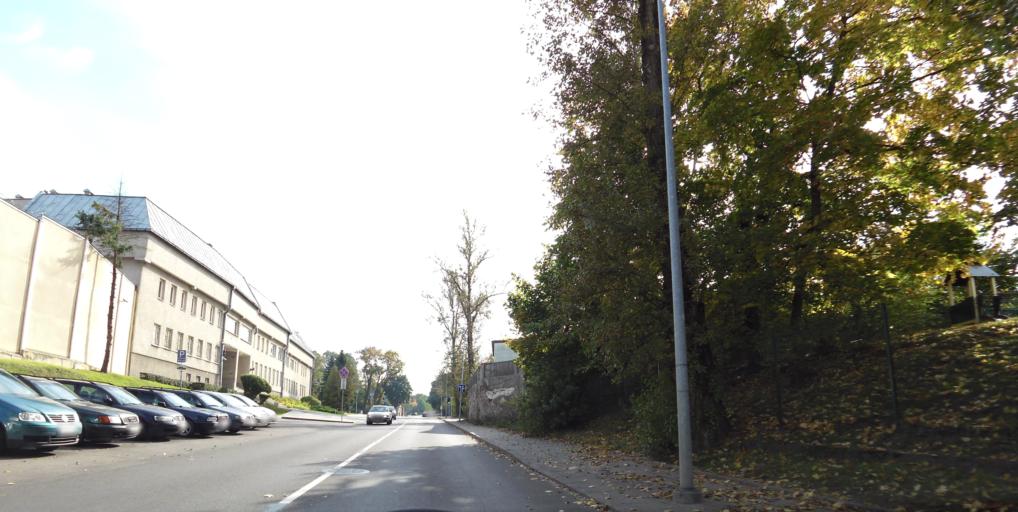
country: LT
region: Vilnius County
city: Rasos
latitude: 54.6746
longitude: 25.2973
